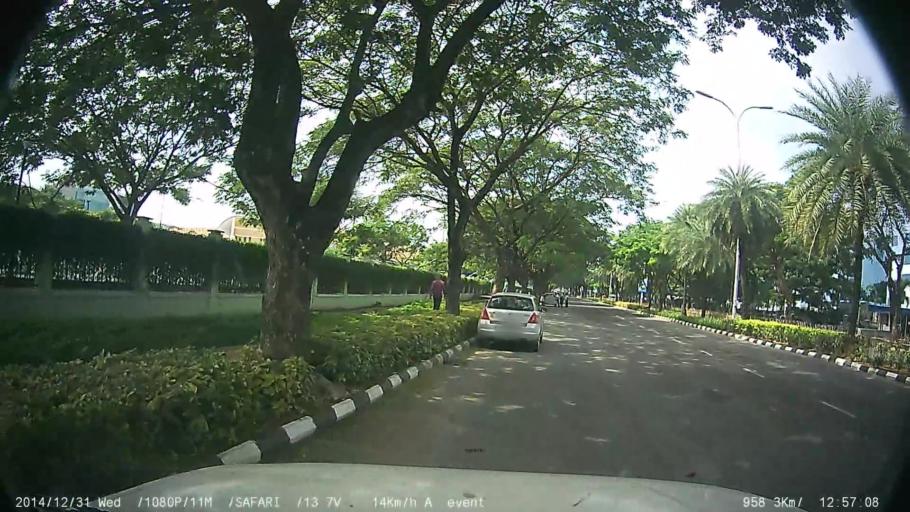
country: IN
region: Tamil Nadu
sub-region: Kancheepuram
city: Singapperumalkovil
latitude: 12.7363
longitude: 80.0069
